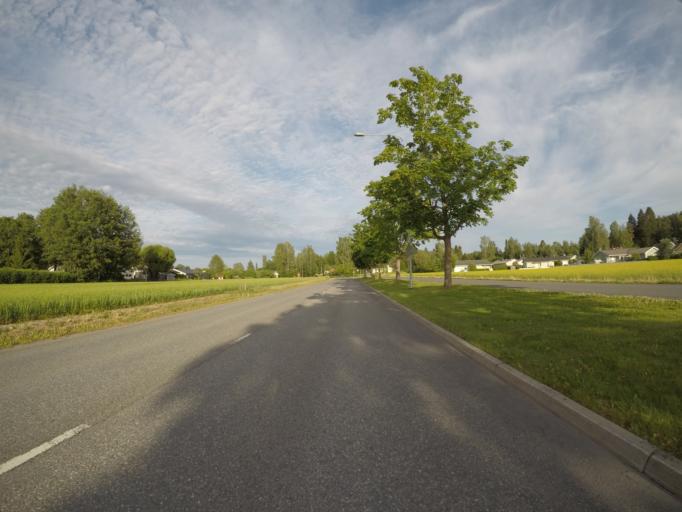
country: FI
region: Haeme
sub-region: Haemeenlinna
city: Haemeenlinna
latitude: 60.9757
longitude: 24.4267
